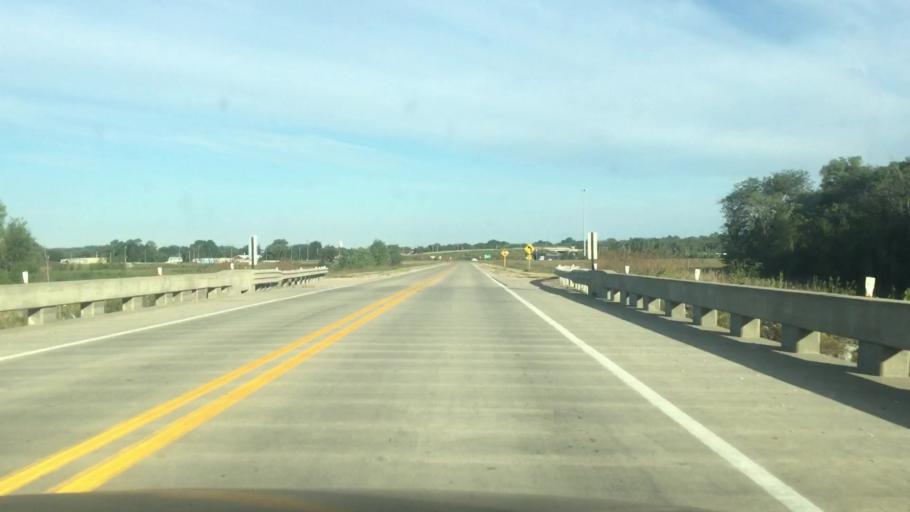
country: US
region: Nebraska
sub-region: Jefferson County
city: Fairbury
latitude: 40.1262
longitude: -97.1640
